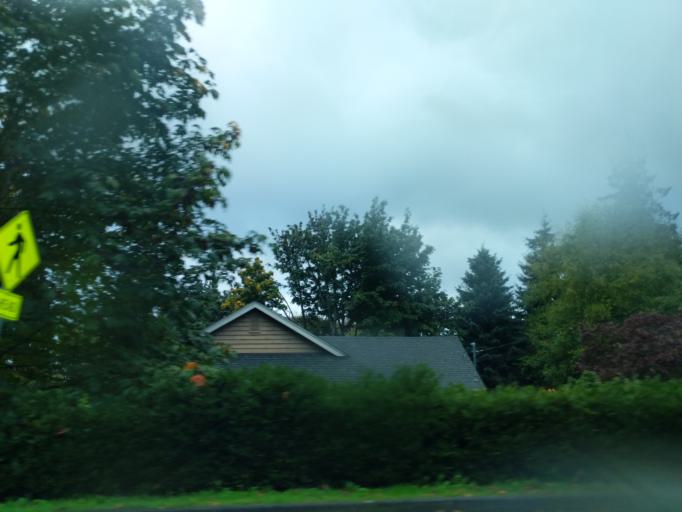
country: US
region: Washington
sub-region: King County
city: Bothell
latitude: 47.7740
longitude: -122.2070
